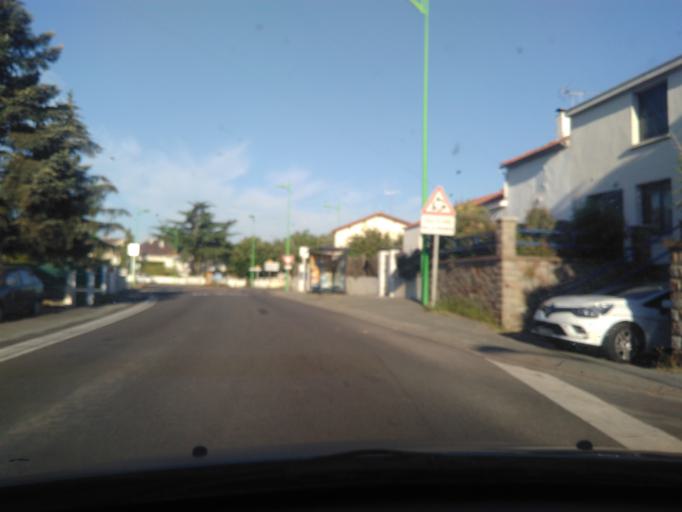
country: FR
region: Pays de la Loire
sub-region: Departement de la Vendee
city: Dompierre-sur-Yon
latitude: 46.7355
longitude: -1.3887
